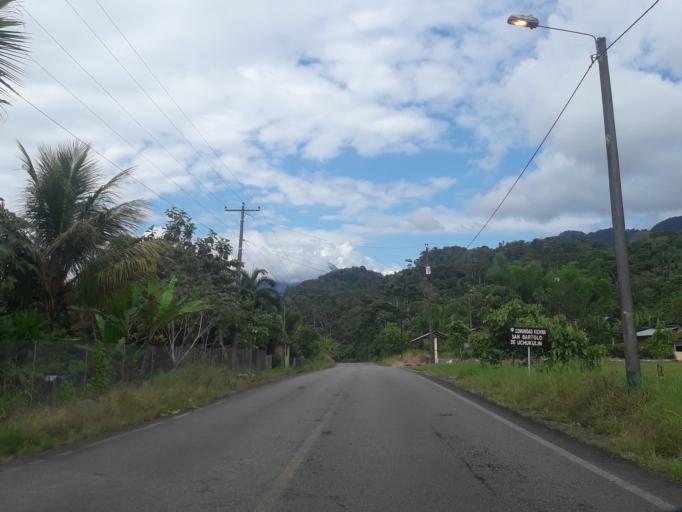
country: EC
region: Napo
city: Tena
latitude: -1.0394
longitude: -77.8952
